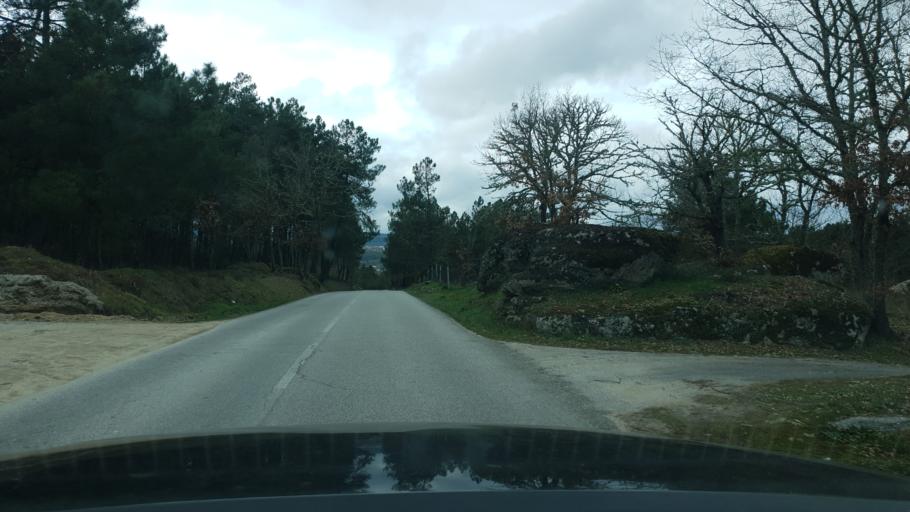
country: PT
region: Viseu
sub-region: Moimenta da Beira
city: Moimenta da Beira
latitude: 40.9832
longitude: -7.5697
